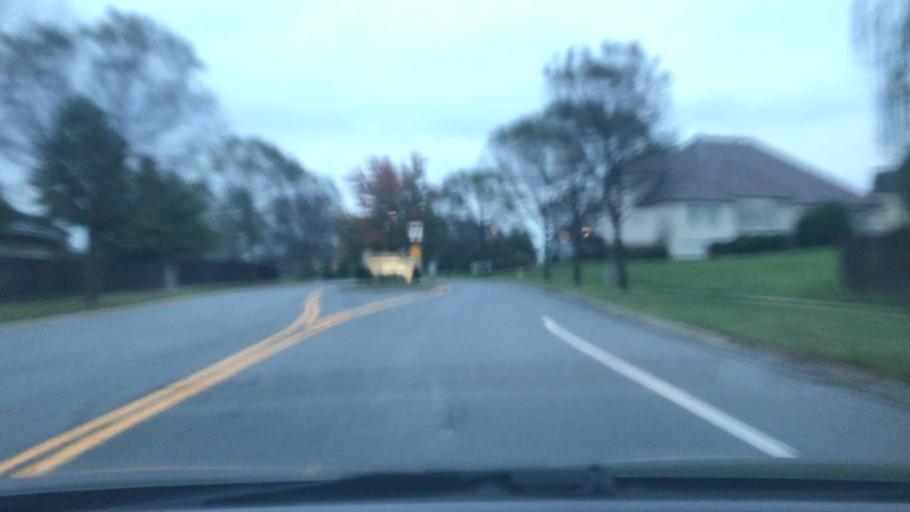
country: US
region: Missouri
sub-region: Jackson County
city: Lees Summit
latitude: 38.9874
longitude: -94.3612
